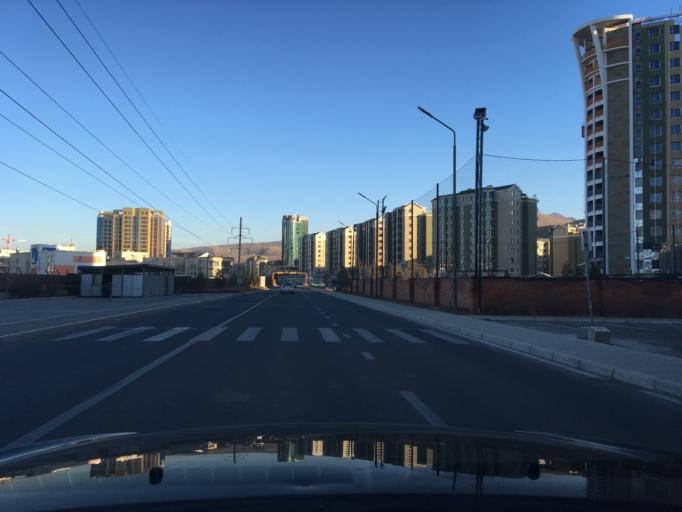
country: MN
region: Ulaanbaatar
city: Ulaanbaatar
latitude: 47.8919
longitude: 106.9271
